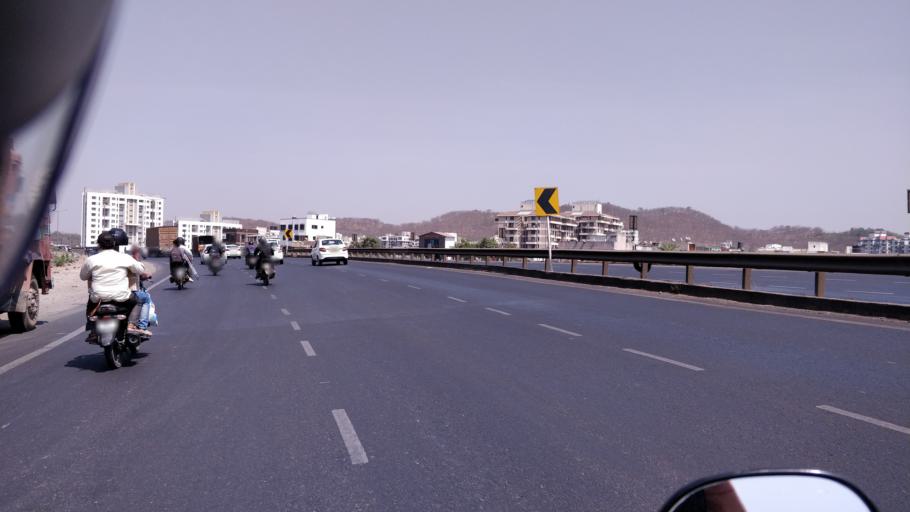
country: IN
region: Maharashtra
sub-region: Pune Division
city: Shivaji Nagar
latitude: 18.5392
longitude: 73.7808
